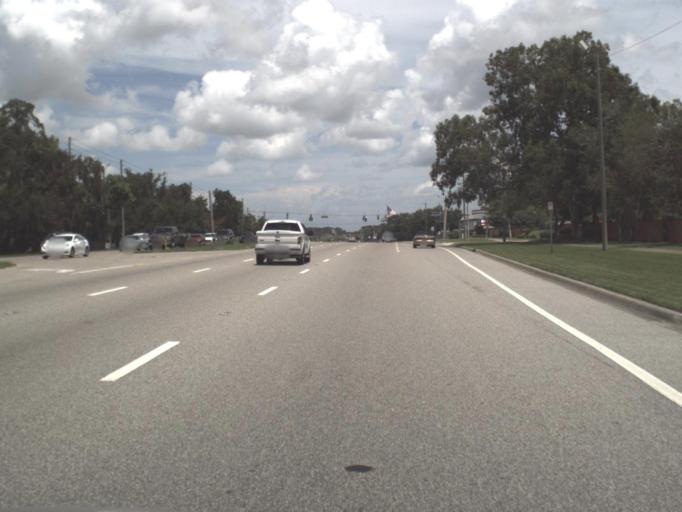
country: US
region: Florida
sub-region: Pinellas County
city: Safety Harbor
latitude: 27.9751
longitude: -82.7088
